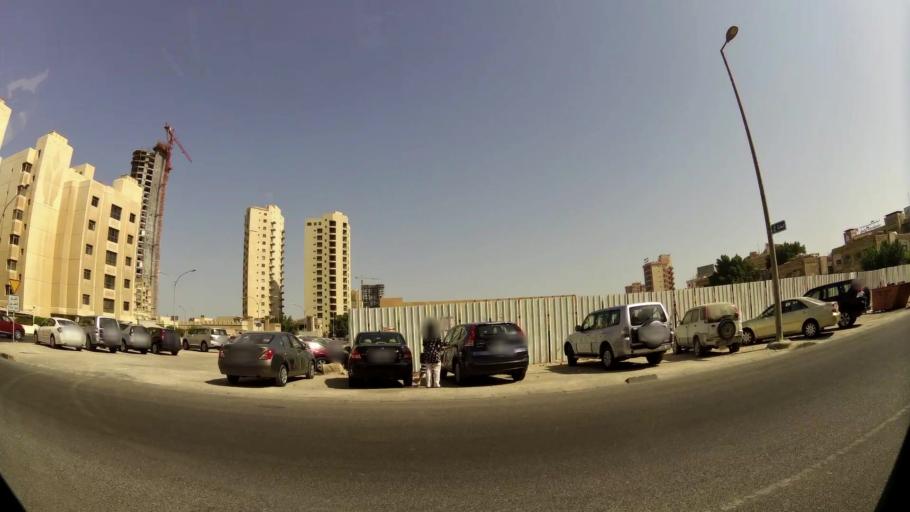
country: KW
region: Muhafazat Hawalli
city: As Salimiyah
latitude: 29.3376
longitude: 48.0615
